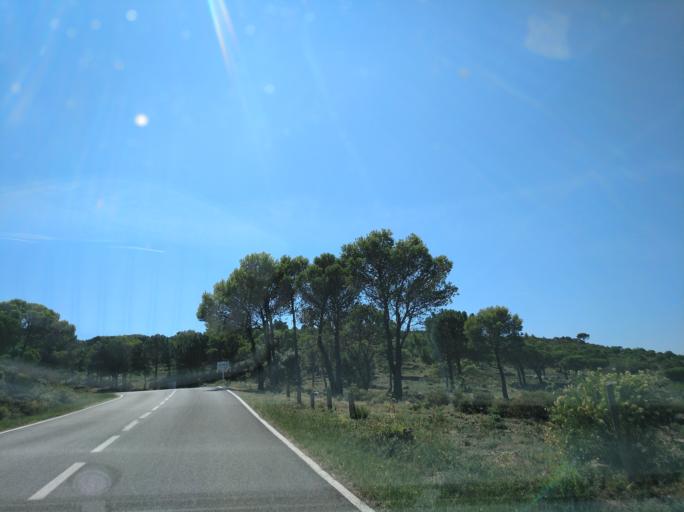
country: ES
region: Catalonia
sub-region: Provincia de Girona
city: Llanca
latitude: 42.3297
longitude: 3.1571
